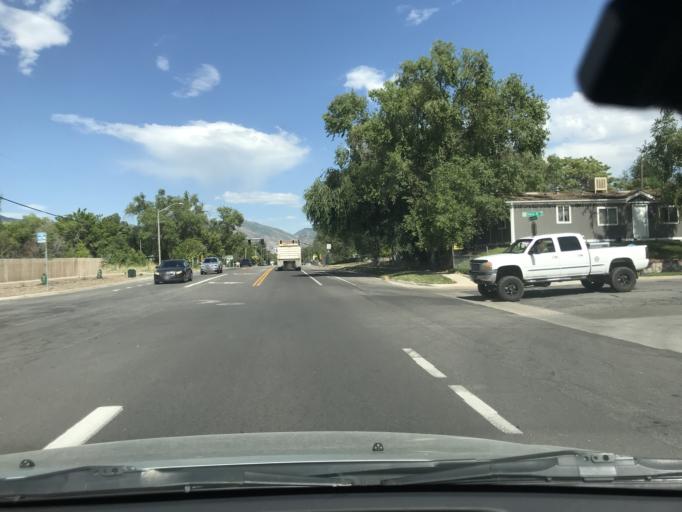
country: US
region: Utah
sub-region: Salt Lake County
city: Salt Lake City
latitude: 40.7606
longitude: -111.9250
